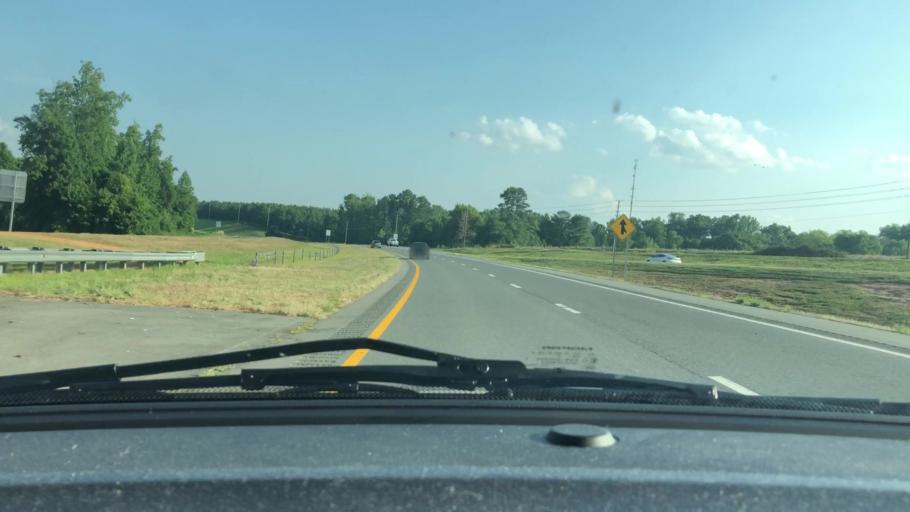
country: US
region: North Carolina
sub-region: Lee County
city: Sanford
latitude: 35.4338
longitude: -79.1228
